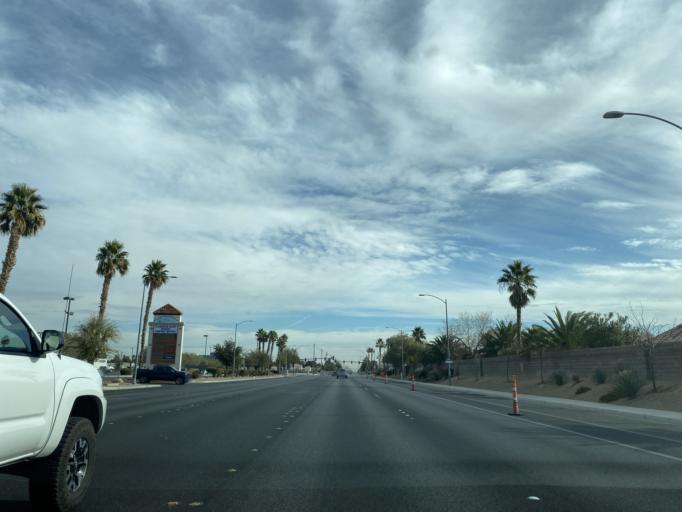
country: US
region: Nevada
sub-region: Clark County
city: Las Vegas
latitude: 36.2466
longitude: -115.2103
